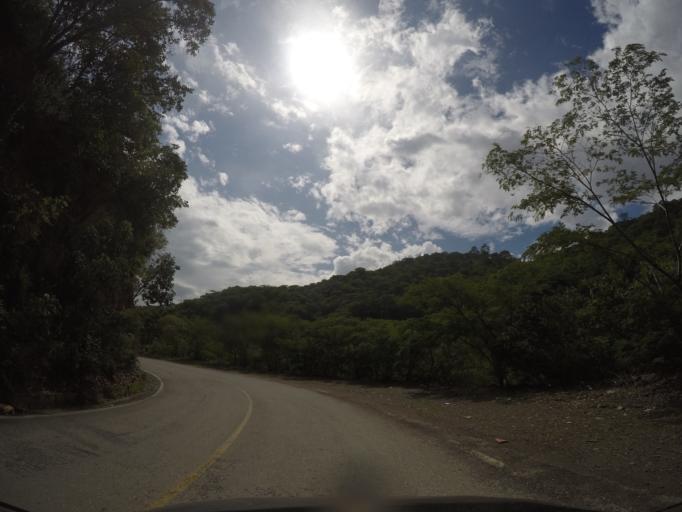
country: MX
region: Oaxaca
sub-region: San Jeronimo Coatlan
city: San Cristobal Honduras
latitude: 16.3728
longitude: -97.0819
